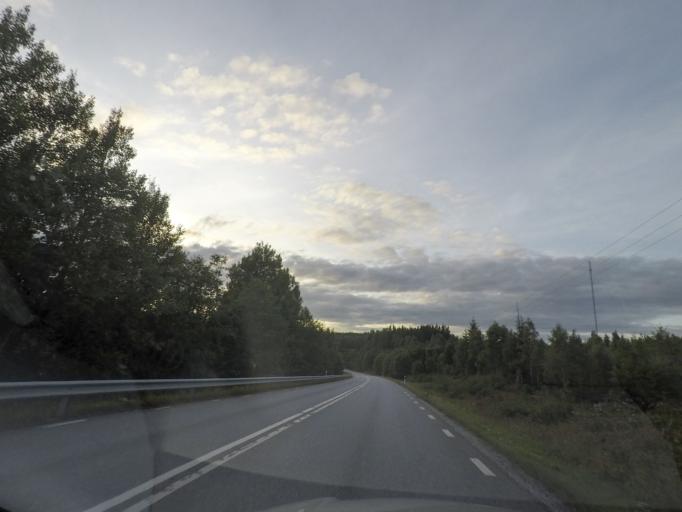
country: SE
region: OErebro
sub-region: Hallefors Kommun
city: Haellefors
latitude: 59.6459
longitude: 14.6001
